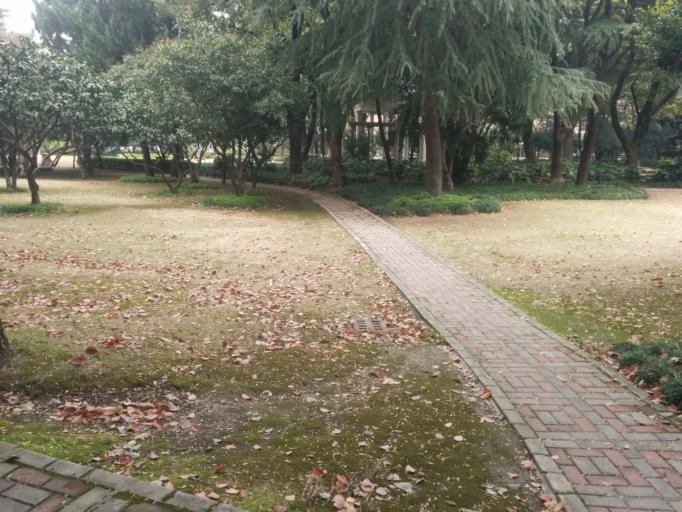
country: CN
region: Shanghai Shi
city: Shanghai
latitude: 31.2202
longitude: 121.4552
